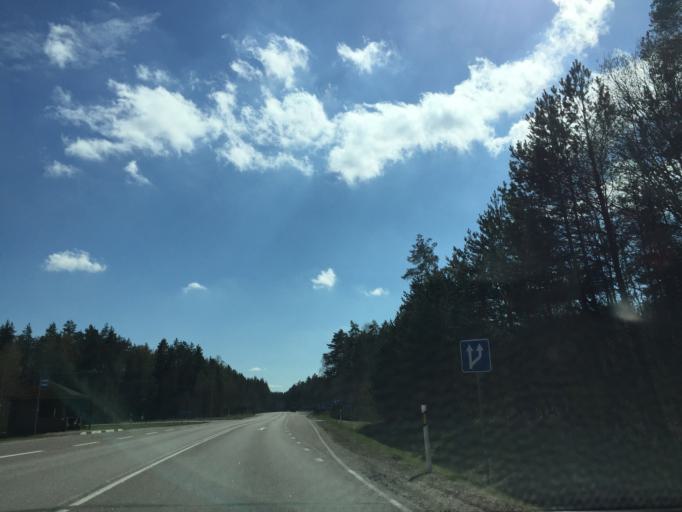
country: EE
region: Valgamaa
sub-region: Torva linn
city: Torva
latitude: 58.0129
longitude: 26.1632
